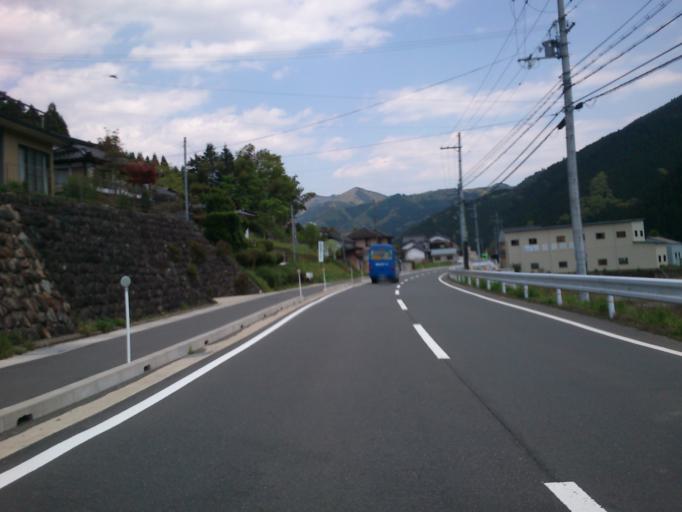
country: JP
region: Kyoto
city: Fukuchiyama
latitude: 35.3449
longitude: 134.9398
